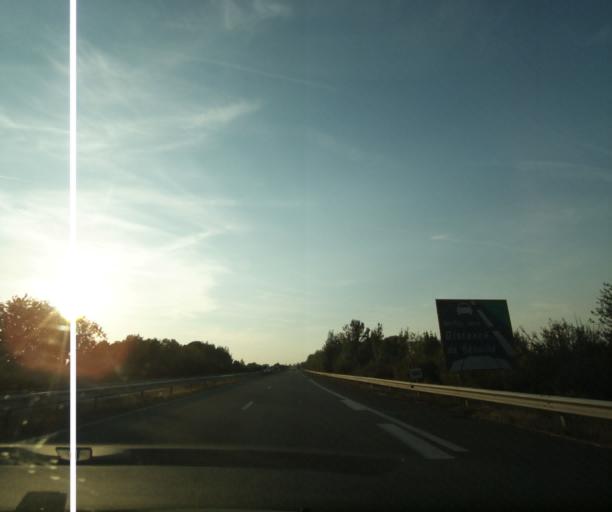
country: FR
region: Midi-Pyrenees
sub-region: Departement du Tarn-et-Garonne
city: Saint-Nicolas-de-la-Grave
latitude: 44.0457
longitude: 0.9926
